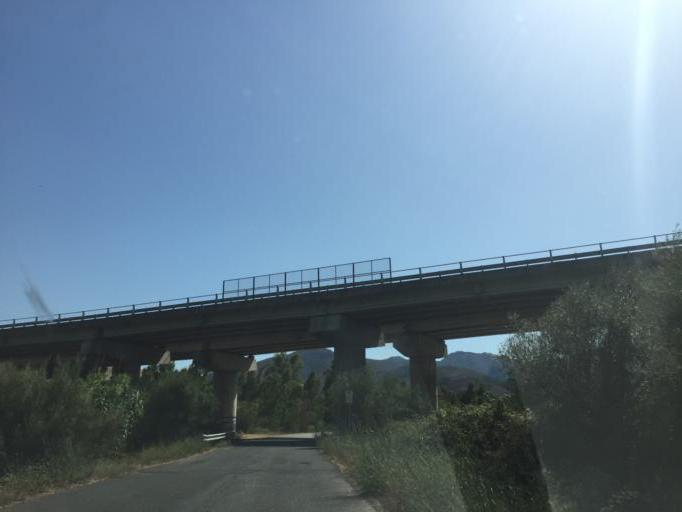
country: IT
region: Sardinia
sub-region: Provincia di Olbia-Tempio
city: San Teodoro
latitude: 40.7303
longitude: 9.6511
